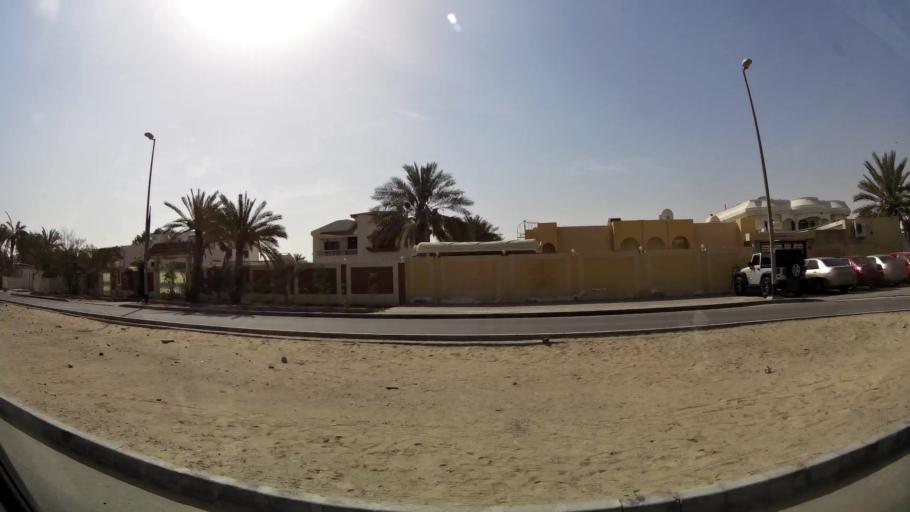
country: AE
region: Ash Shariqah
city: Sharjah
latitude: 25.2627
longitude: 55.3977
